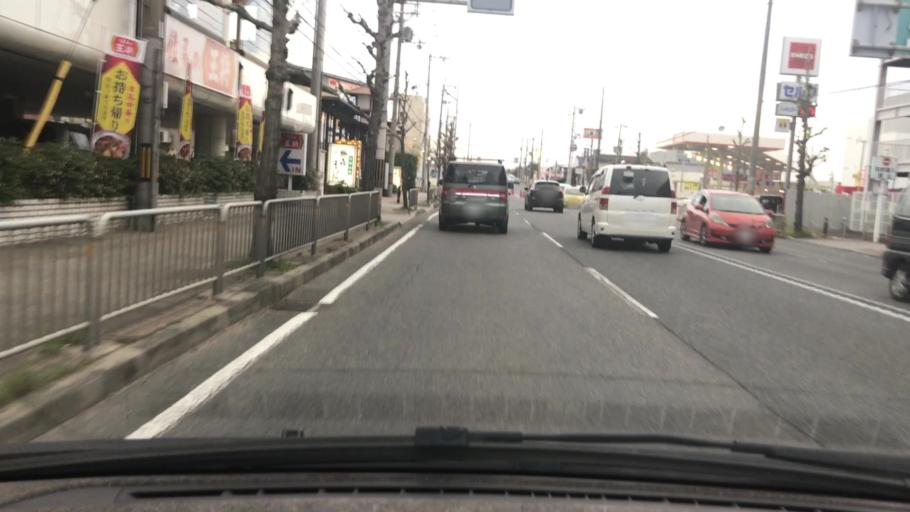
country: JP
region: Kyoto
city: Muko
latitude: 34.9586
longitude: 135.7458
